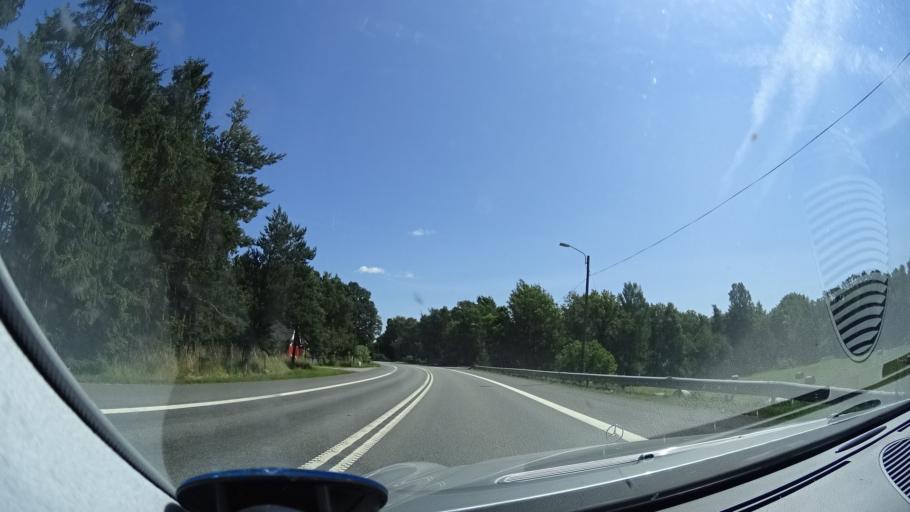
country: SE
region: Skane
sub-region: Kristianstads Kommun
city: Onnestad
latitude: 55.9297
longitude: 13.9295
